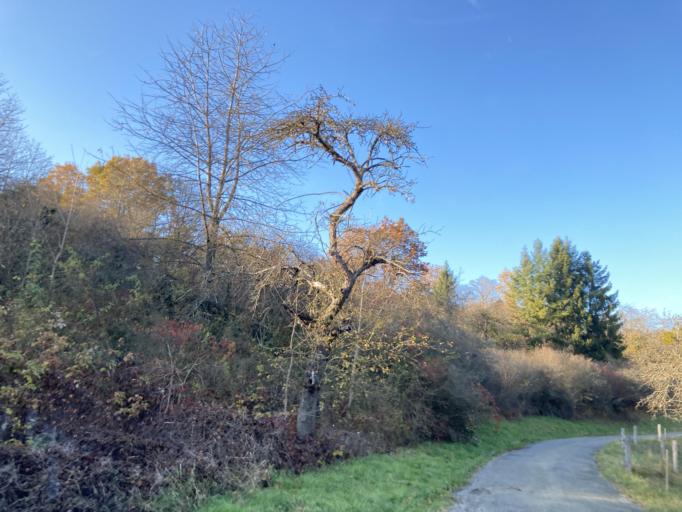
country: DE
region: Baden-Wuerttemberg
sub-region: Tuebingen Region
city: Rottenburg
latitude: 48.5383
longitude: 8.9769
